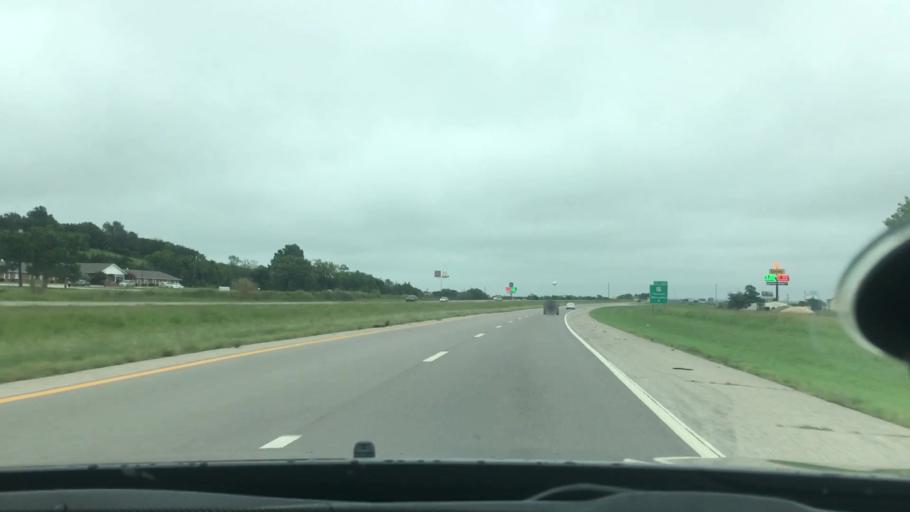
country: US
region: Oklahoma
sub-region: Okfuskee County
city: Okemah
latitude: 35.4211
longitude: -96.3078
